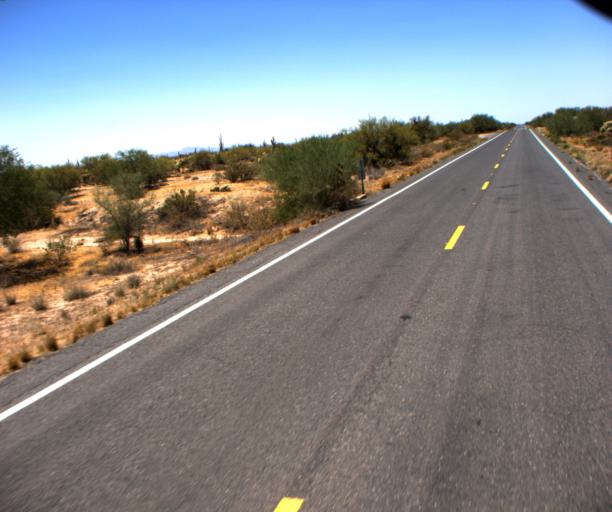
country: US
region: Arizona
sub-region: Pinal County
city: Florence
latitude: 32.8658
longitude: -111.2453
